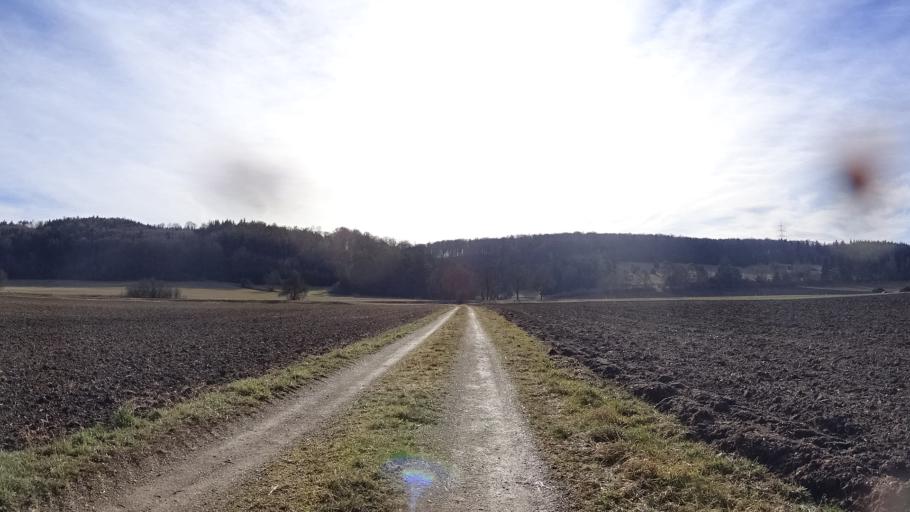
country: DE
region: Bavaria
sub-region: Upper Bavaria
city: Walting
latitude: 48.9025
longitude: 11.2904
